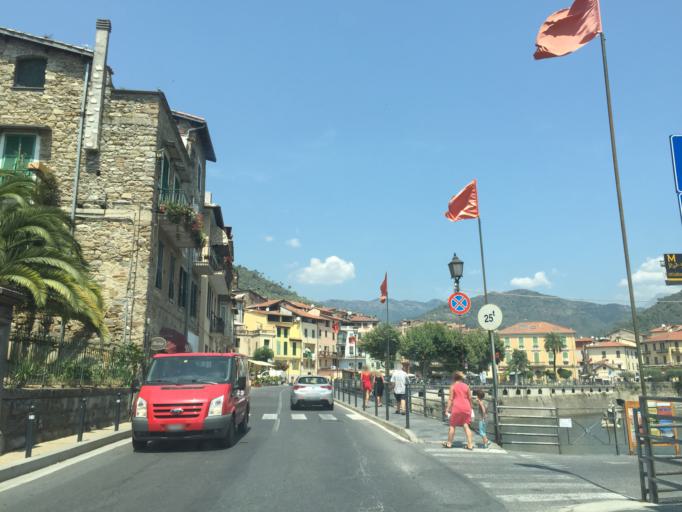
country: IT
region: Liguria
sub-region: Provincia di Imperia
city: Dolceacqua
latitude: 43.8500
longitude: 7.6232
